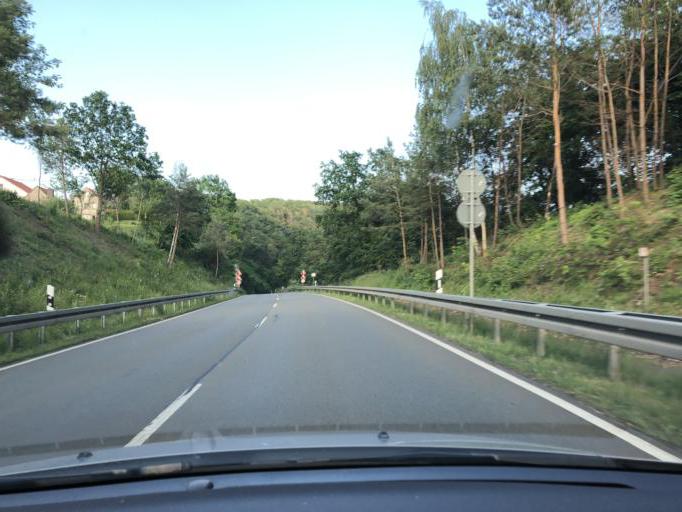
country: DE
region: Hesse
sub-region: Regierungsbezirk Kassel
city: Guxhagen
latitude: 51.1979
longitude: 9.4863
